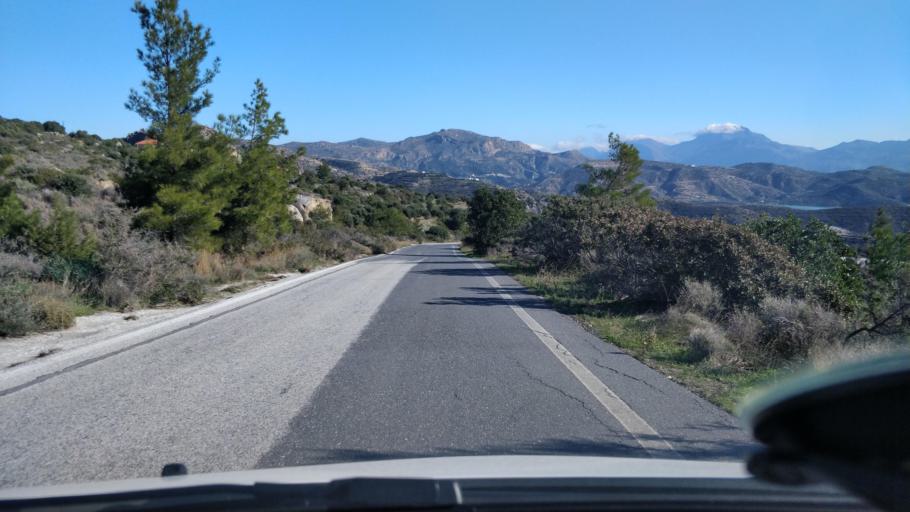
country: GR
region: Crete
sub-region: Nomos Lasithiou
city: Gra Liyia
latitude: 35.0361
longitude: 25.6630
